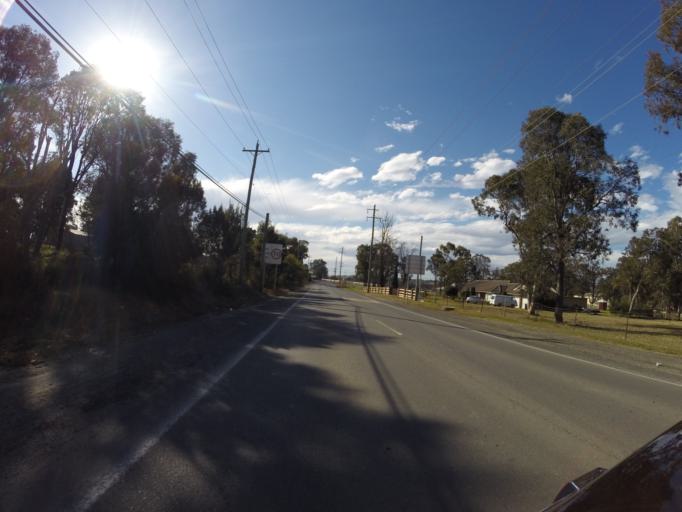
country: AU
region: New South Wales
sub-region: Fairfield
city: Cecil Park
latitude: -33.8822
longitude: 150.7924
